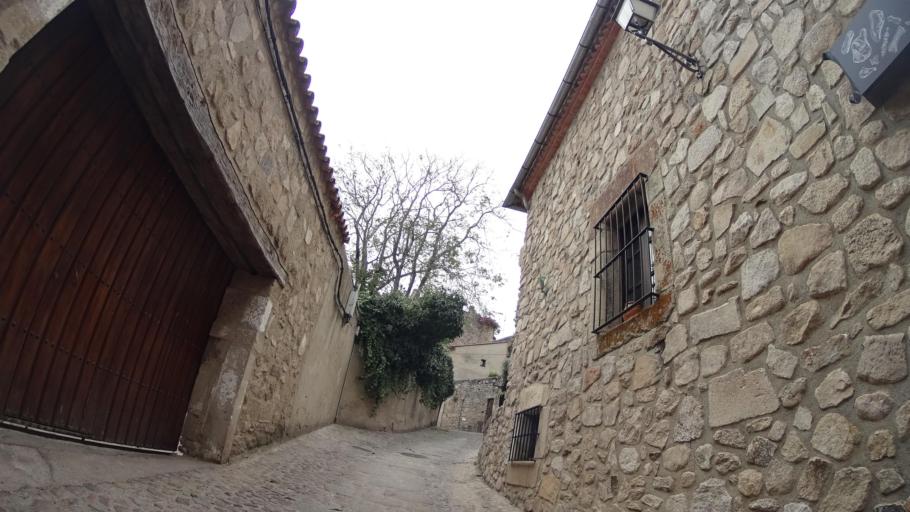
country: ES
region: Extremadura
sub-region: Provincia de Caceres
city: Trujillo
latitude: 39.4610
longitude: -5.8823
